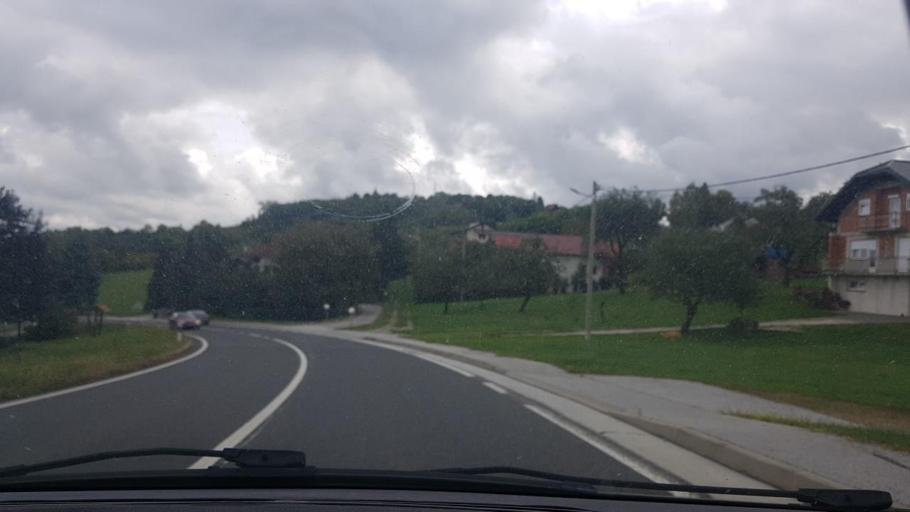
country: SI
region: Bistrica ob Sotli
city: Bistrica ob Sotli
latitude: 46.0628
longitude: 15.7570
